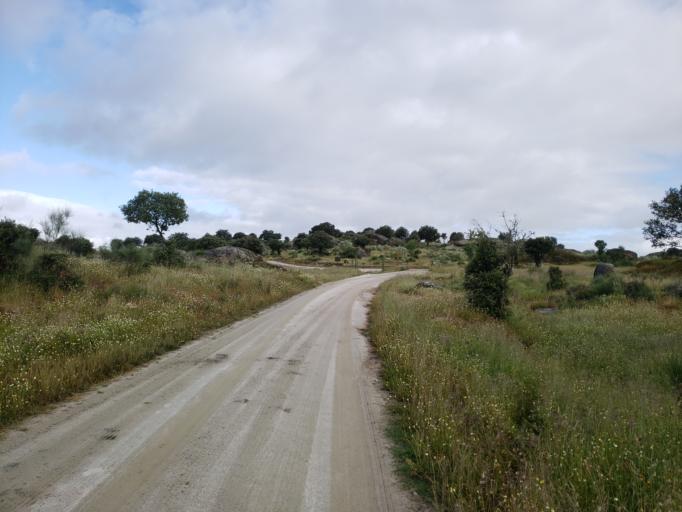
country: ES
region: Extremadura
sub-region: Provincia de Caceres
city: Malpartida de Caceres
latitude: 39.4264
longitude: -6.4931
